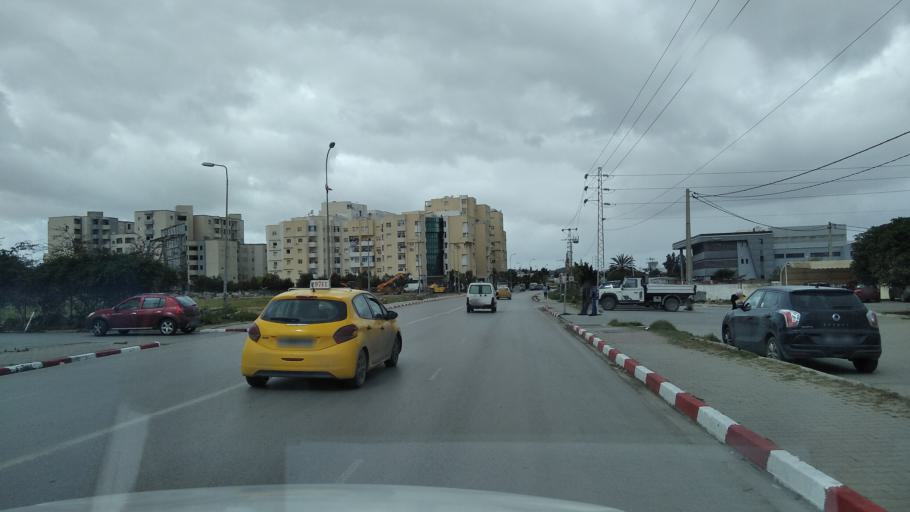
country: TN
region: Bin 'Arus
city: Ben Arous
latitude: 36.7468
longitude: 10.2316
